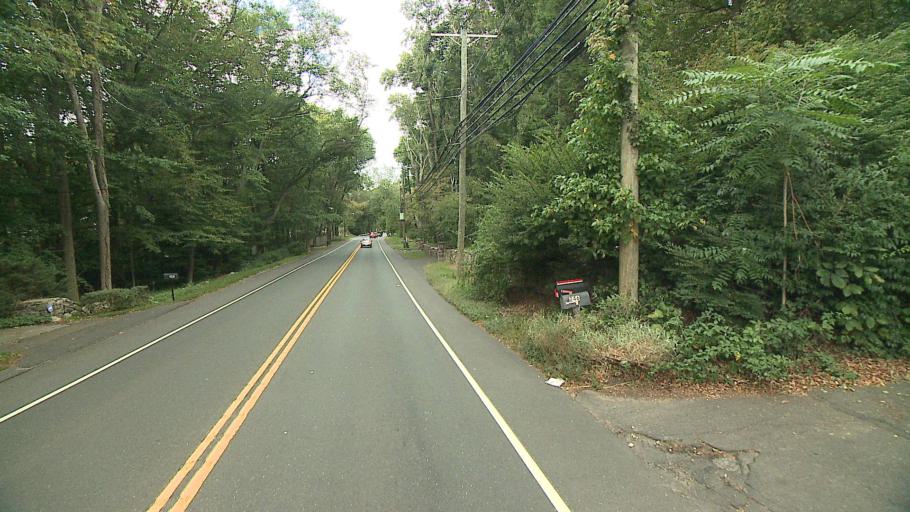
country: US
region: Connecticut
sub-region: Fairfield County
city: Westport
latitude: 41.1570
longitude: -73.3728
